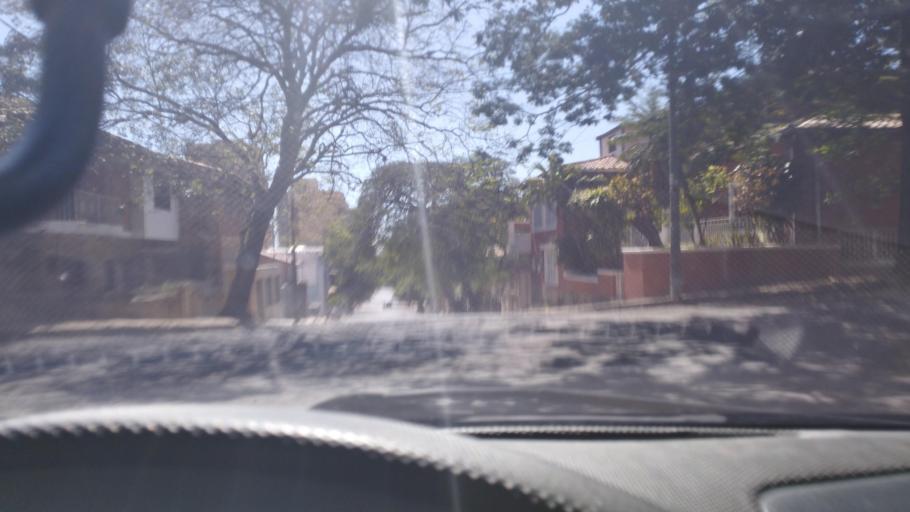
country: PY
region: Asuncion
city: Asuncion
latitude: -25.2947
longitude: -57.6128
